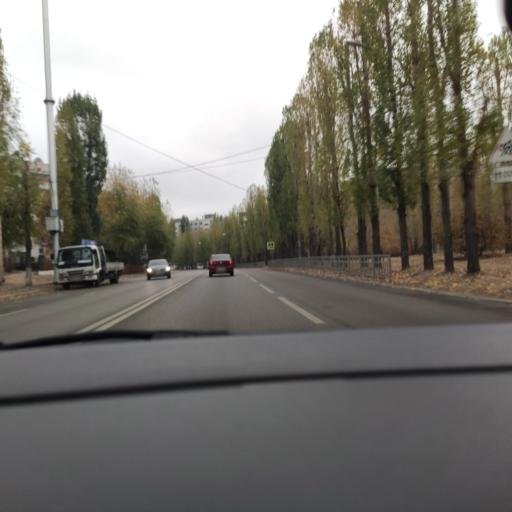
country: RU
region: Voronezj
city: Podgornoye
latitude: 51.7069
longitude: 39.1431
